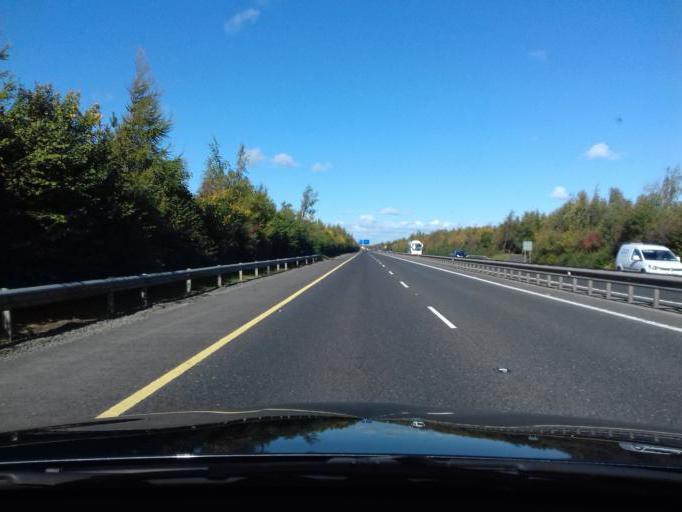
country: IE
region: Leinster
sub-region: An Mhi
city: Ashbourne
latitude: 53.4715
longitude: -6.3658
